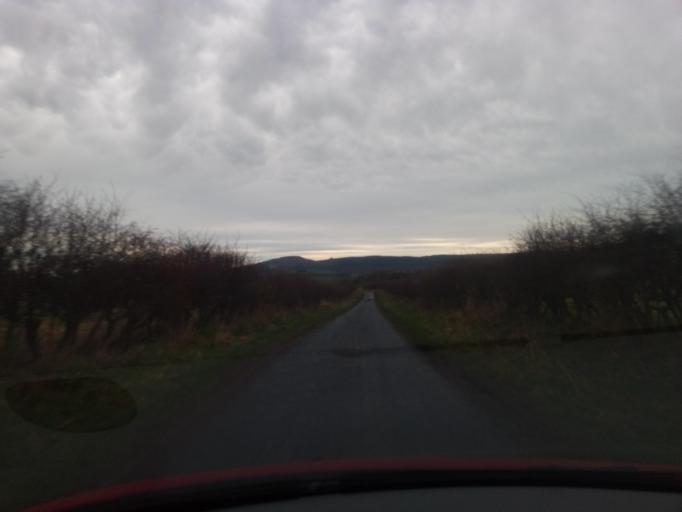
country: GB
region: England
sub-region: Northumberland
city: Wooler
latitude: 55.5021
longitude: -1.9387
